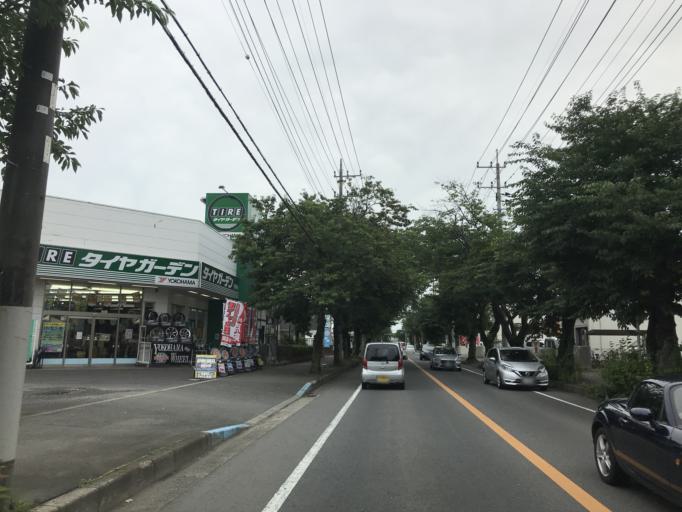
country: JP
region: Ibaraki
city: Mito-shi
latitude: 36.3302
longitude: 140.4592
